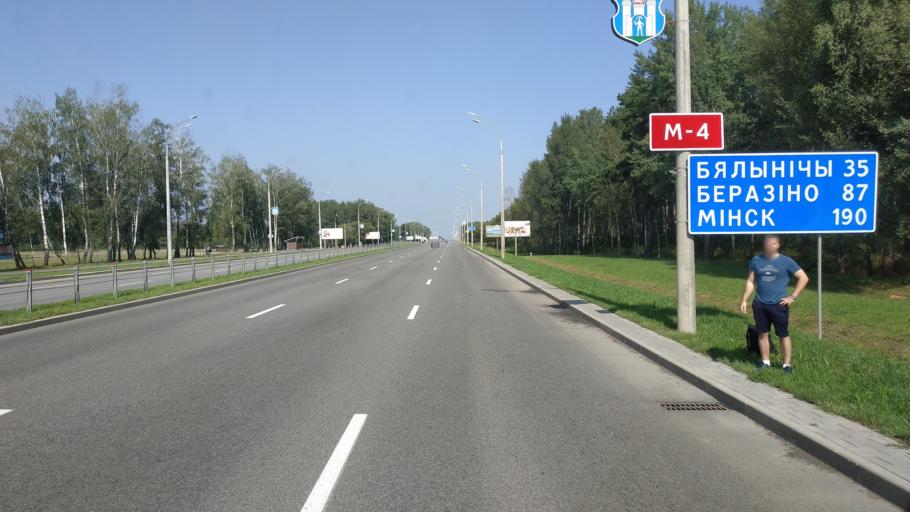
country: BY
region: Mogilev
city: Buynichy
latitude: 53.9381
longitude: 30.2468
